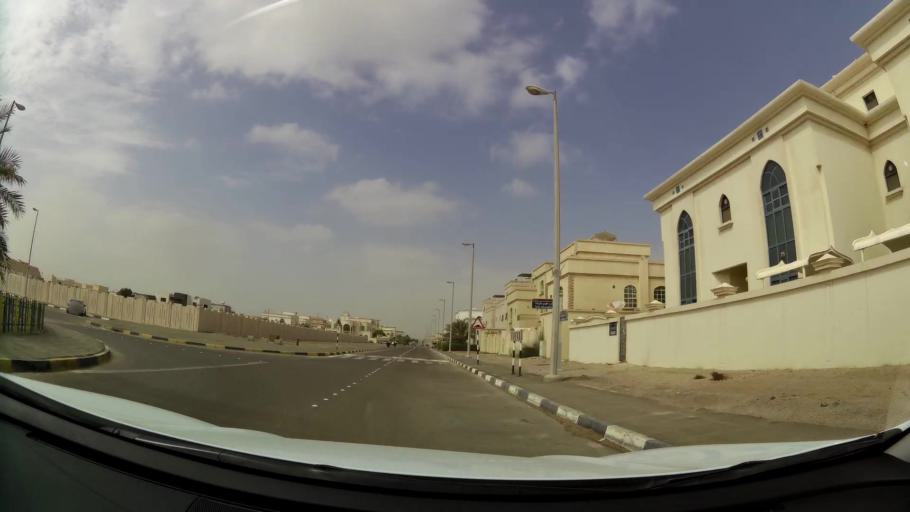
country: AE
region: Abu Dhabi
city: Abu Dhabi
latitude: 24.3949
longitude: 54.4984
